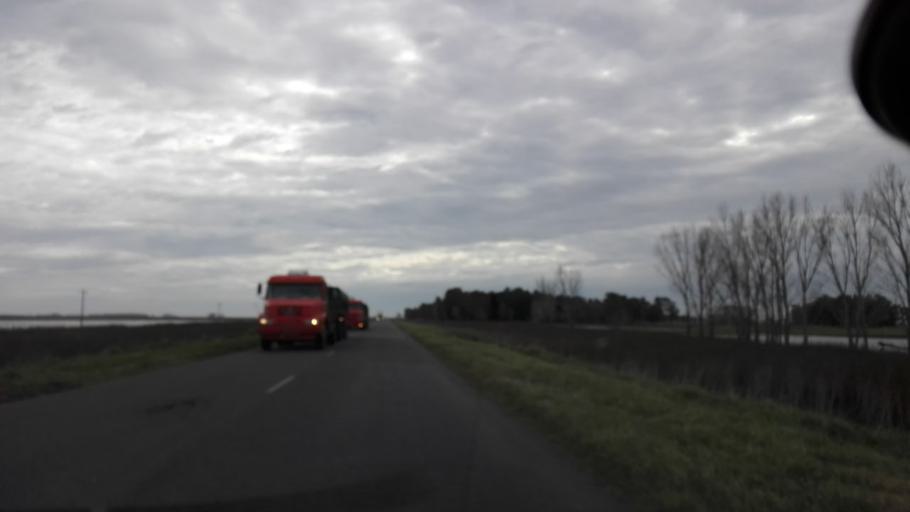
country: AR
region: Buenos Aires
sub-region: Partido de Las Flores
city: Las Flores
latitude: -36.3358
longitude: -59.0175
